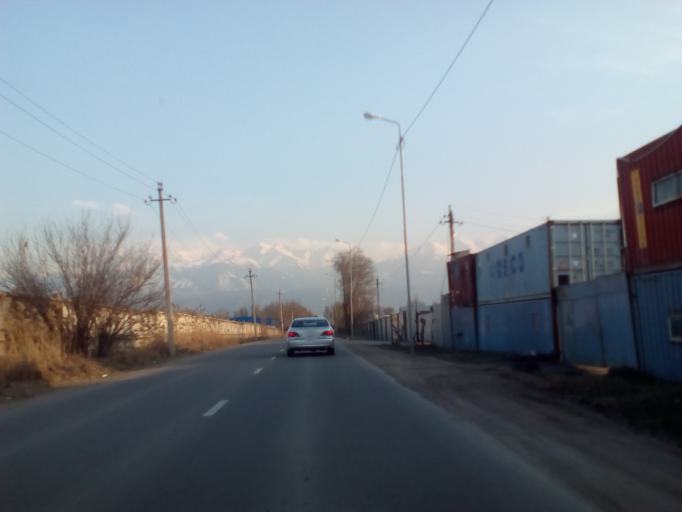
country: KZ
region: Almaty Oblysy
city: Burunday
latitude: 43.2326
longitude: 76.7409
